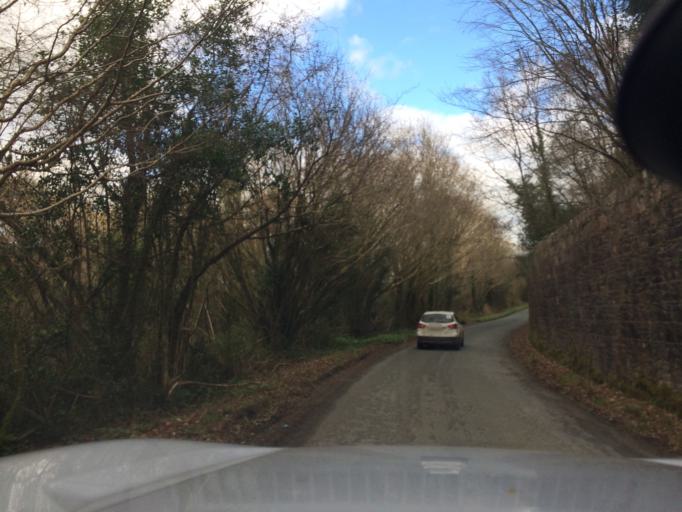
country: IE
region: Munster
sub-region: Waterford
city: Portlaw
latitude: 52.2834
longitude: -7.3210
